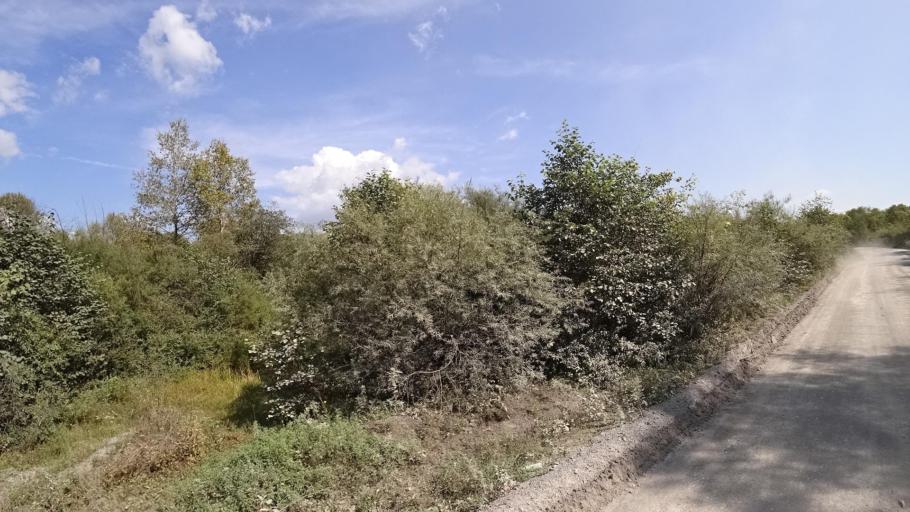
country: RU
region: Jewish Autonomous Oblast
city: Londoko
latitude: 49.0228
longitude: 131.9279
